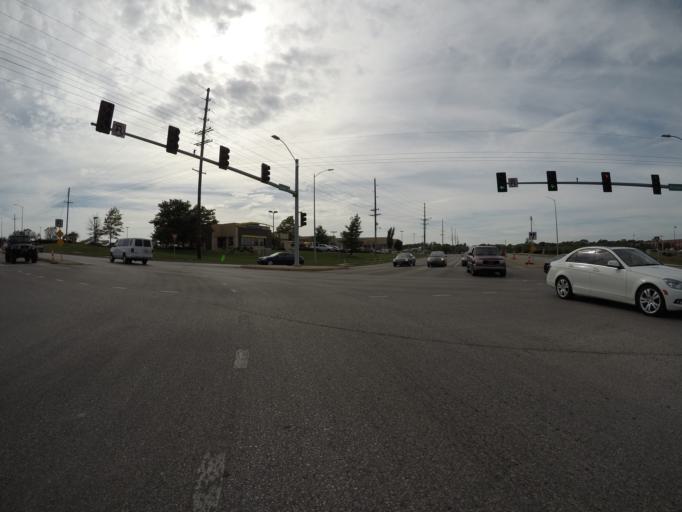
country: US
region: Kansas
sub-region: Johnson County
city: Olathe
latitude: 38.8837
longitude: -94.8345
